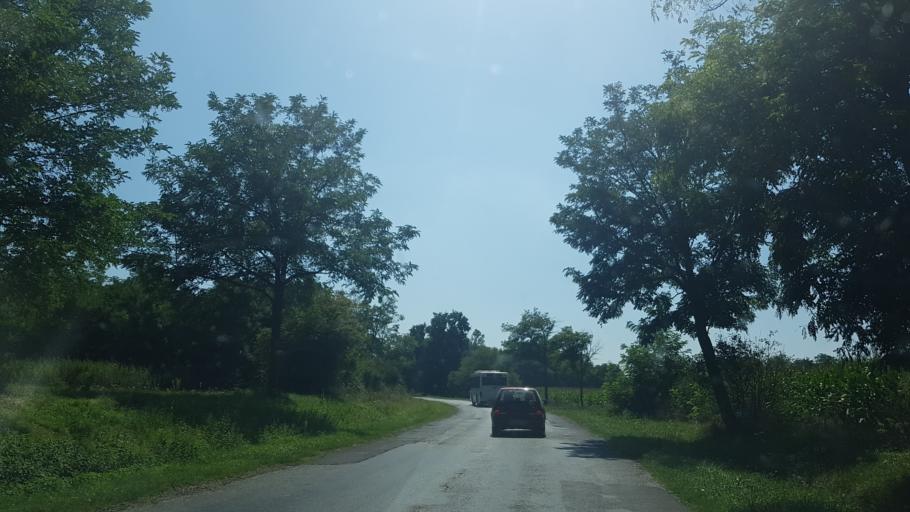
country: HU
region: Somogy
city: Segesd
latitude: 46.3022
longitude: 17.2930
